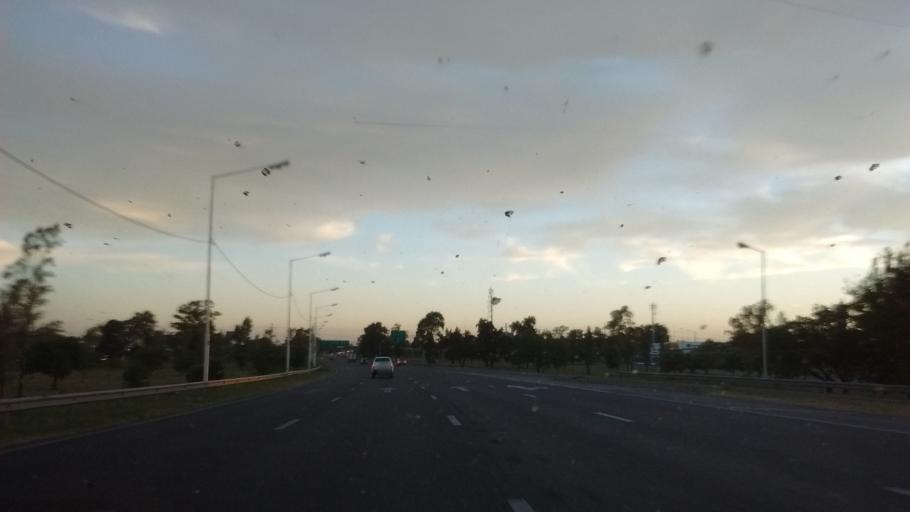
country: AR
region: Santa Fe
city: Granadero Baigorria
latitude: -32.9035
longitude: -60.7250
